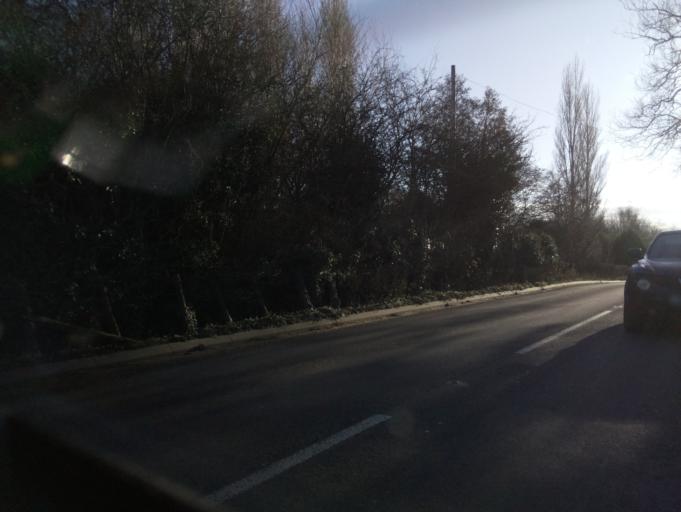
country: GB
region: England
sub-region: Derbyshire
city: Rodsley
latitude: 52.8715
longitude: -1.7607
